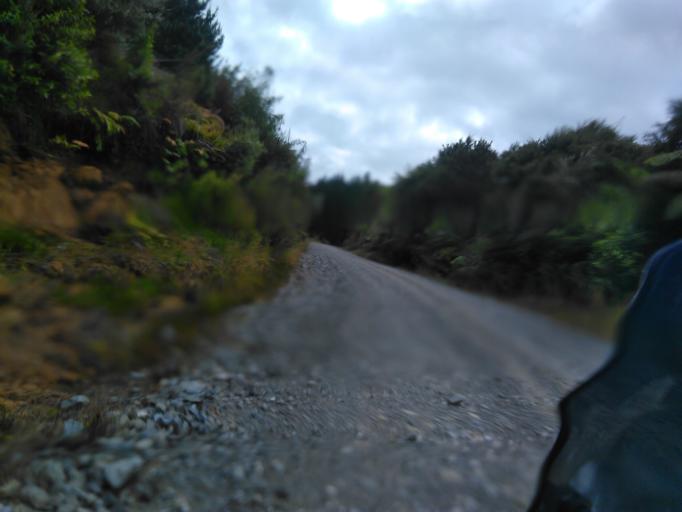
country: NZ
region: Gisborne
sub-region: Gisborne District
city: Gisborne
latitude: -38.1854
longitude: 178.1096
